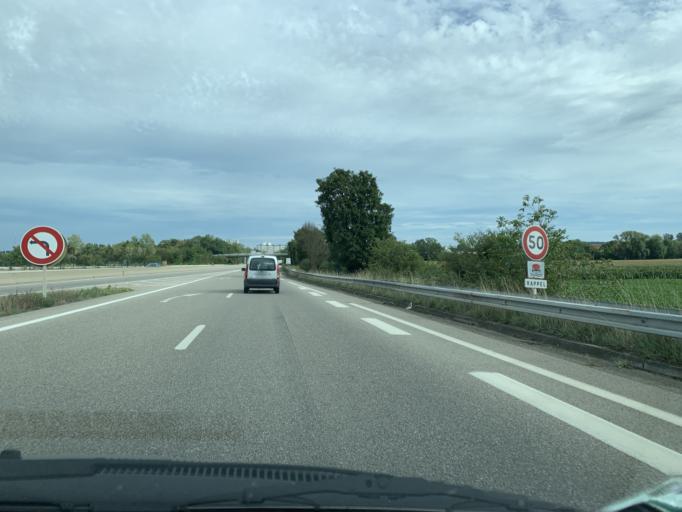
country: FR
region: Alsace
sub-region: Departement du Haut-Rhin
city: Lutterbach
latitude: 47.7443
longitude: 7.2793
